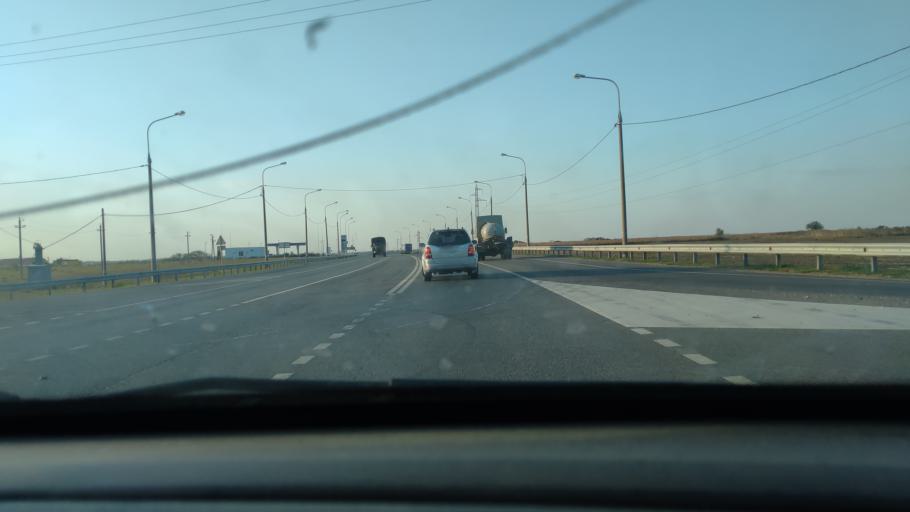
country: RU
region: Krasnodarskiy
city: Kanevskaya
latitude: 46.0769
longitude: 39.0144
